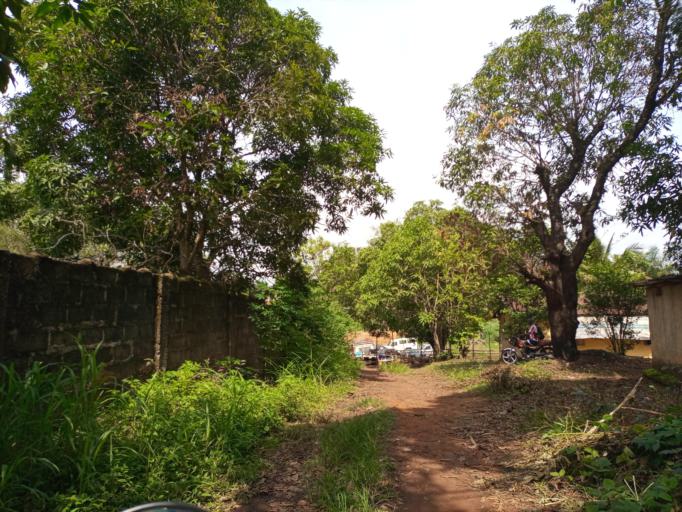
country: SL
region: Southern Province
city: Bo
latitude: 7.9736
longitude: -11.7607
